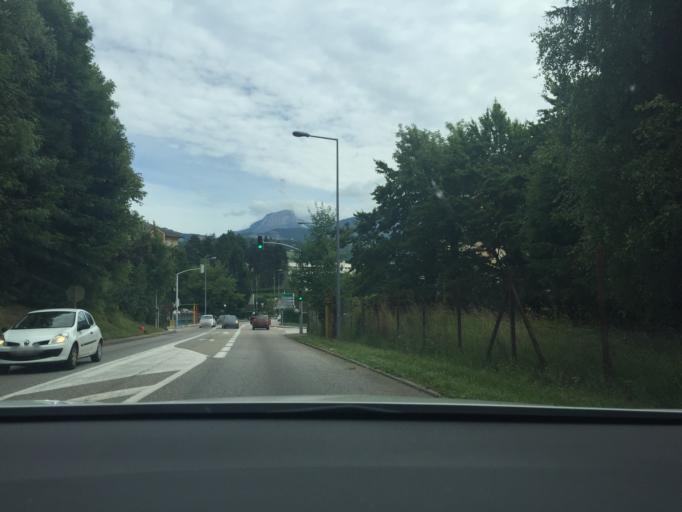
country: FR
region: Rhone-Alpes
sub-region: Departement de la Savoie
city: Cognin
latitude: 45.5652
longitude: 5.9032
